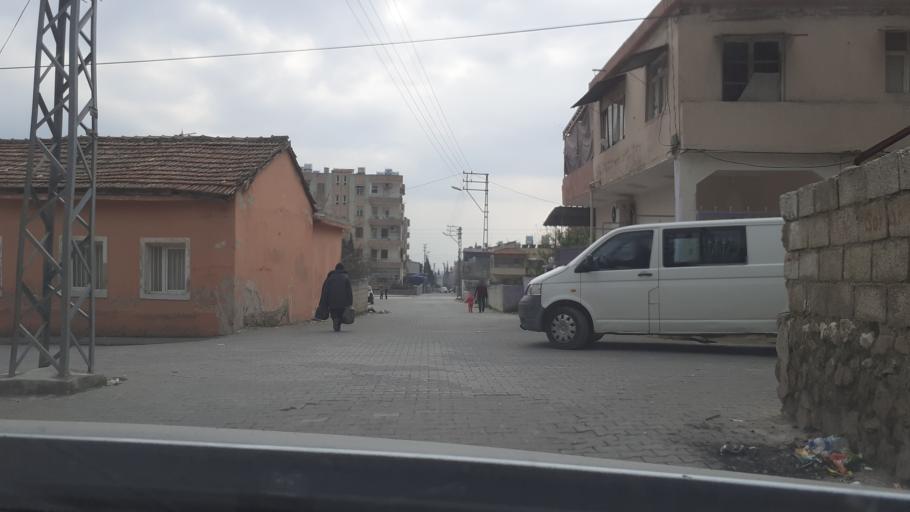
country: TR
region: Hatay
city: Kirikhan
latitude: 36.4950
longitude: 36.3527
